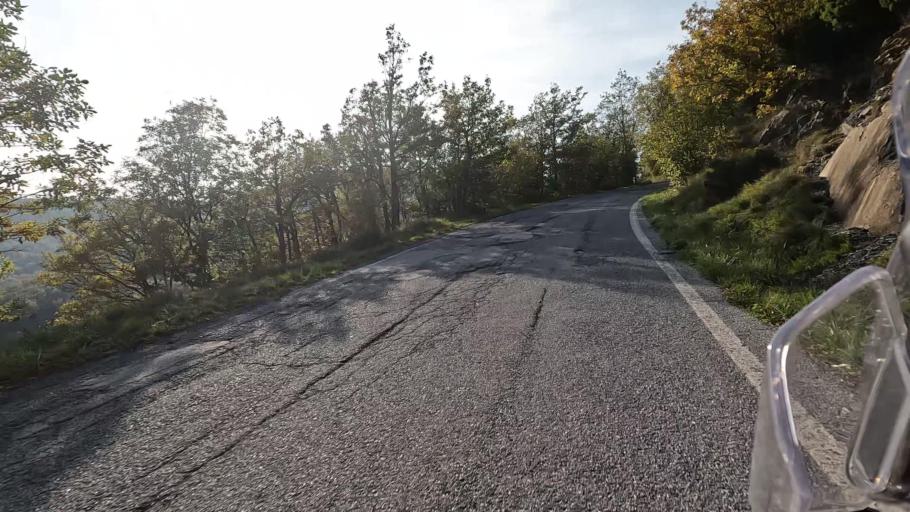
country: IT
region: Liguria
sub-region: Provincia di Savona
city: Urbe
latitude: 44.4763
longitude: 8.5701
